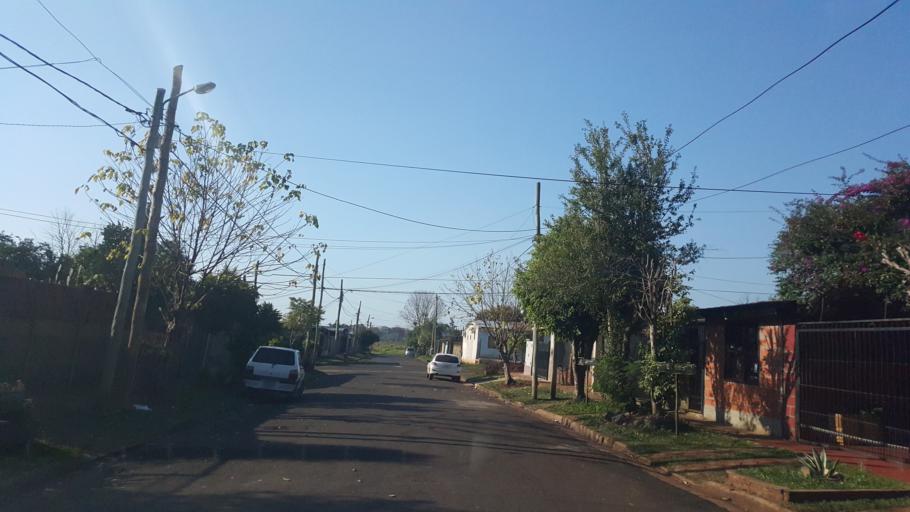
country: AR
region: Misiones
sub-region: Departamento de Capital
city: Posadas
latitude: -27.4048
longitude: -55.9562
